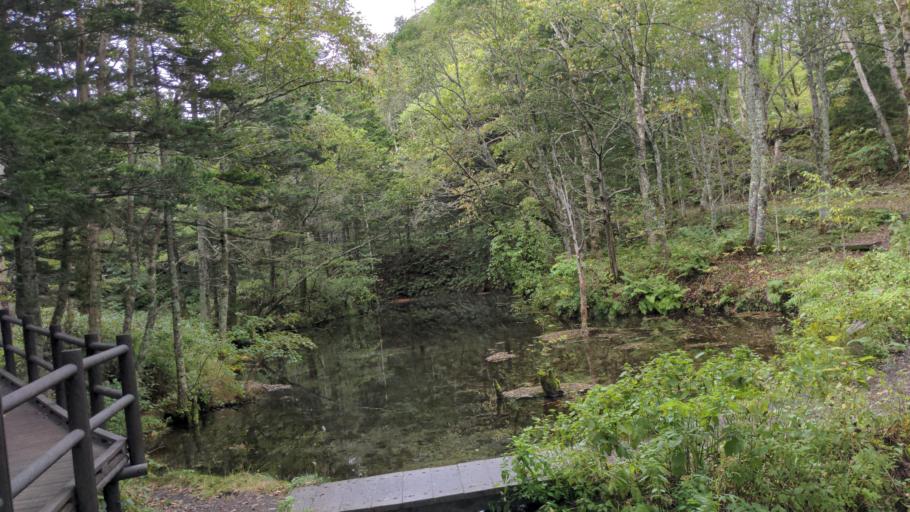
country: JP
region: Hokkaido
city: Abashiri
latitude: 43.6455
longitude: 144.5498
